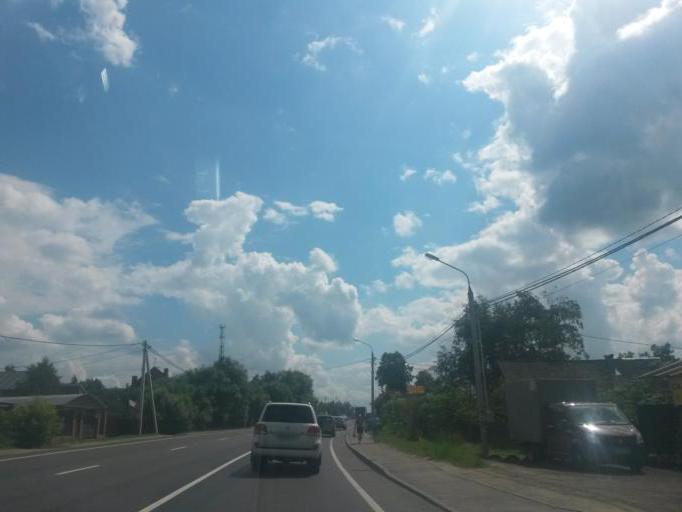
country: RU
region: Moskovskaya
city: Vostryakovo
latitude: 55.3909
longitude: 37.7885
